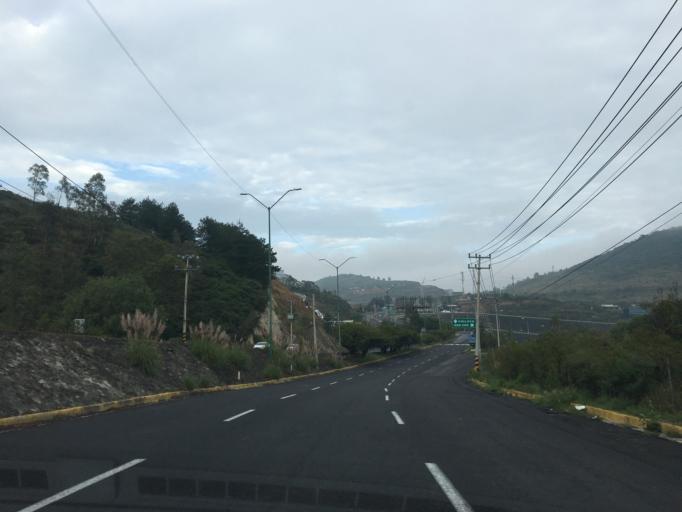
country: MX
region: Mexico
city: Ciudad Lopez Mateos
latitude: 19.5447
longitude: -99.2697
